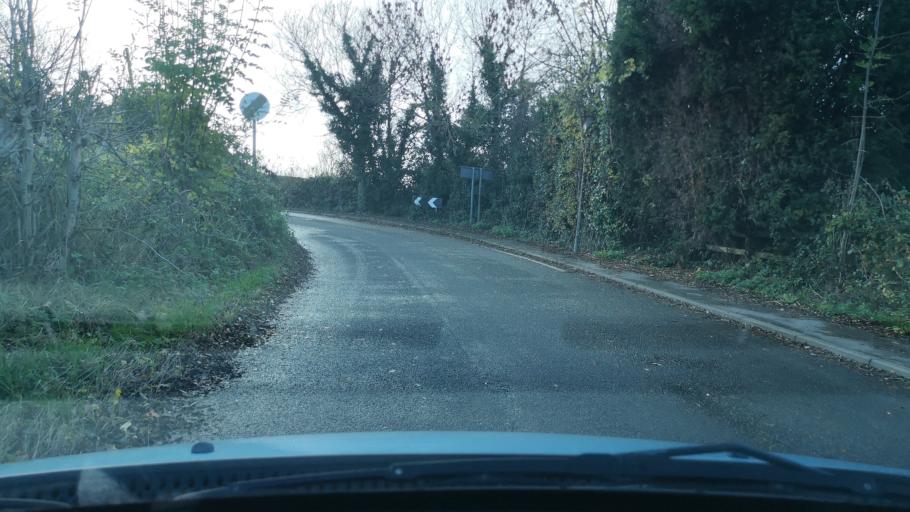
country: GB
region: England
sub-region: City and Borough of Wakefield
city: Ryhill
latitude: 53.6358
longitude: -1.4242
